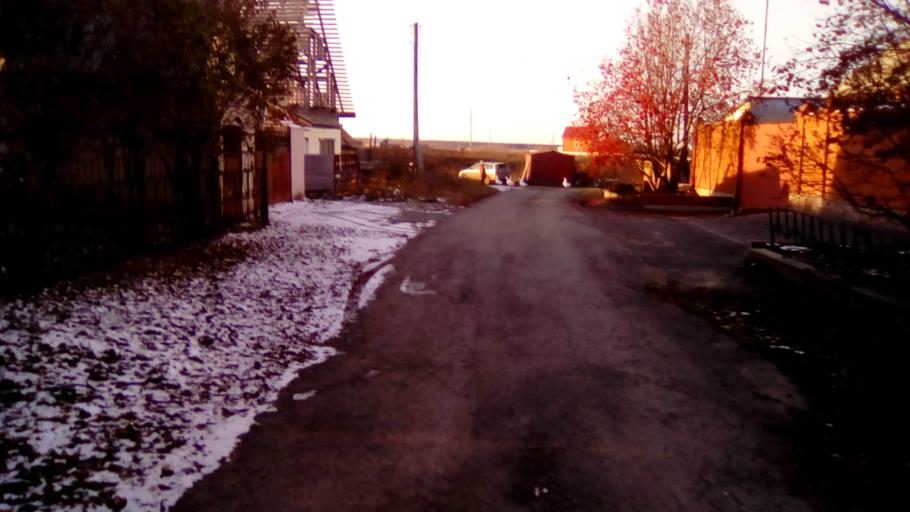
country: RU
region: Tjumen
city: Moskovskiy
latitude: 57.2225
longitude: 65.3635
